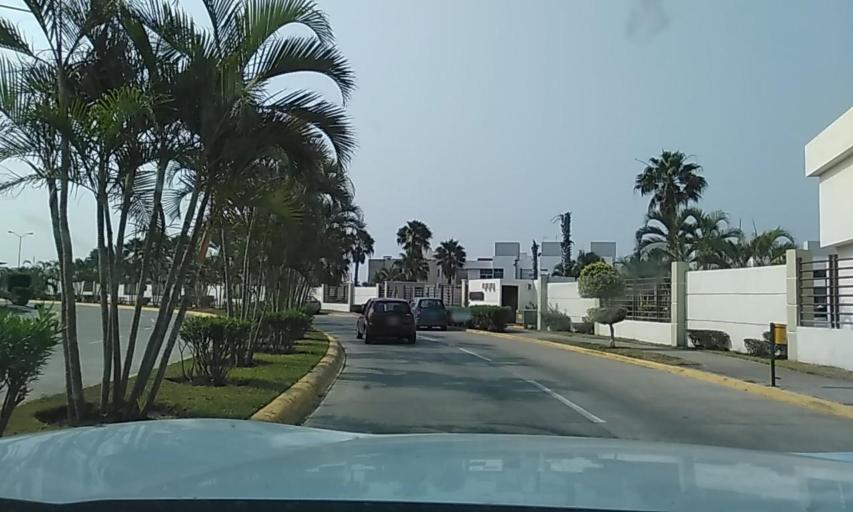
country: MX
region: Veracruz
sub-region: Veracruz
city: Hacienda Sotavento
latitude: 19.1314
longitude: -96.1728
